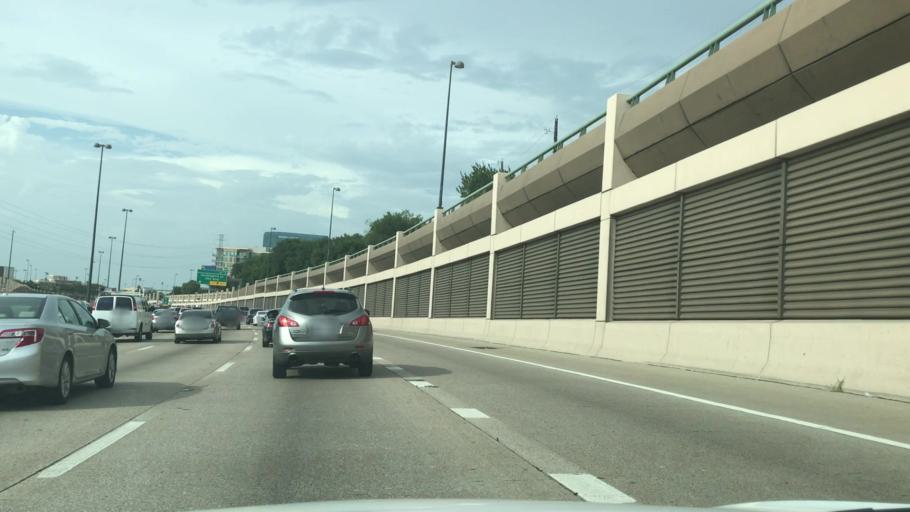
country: US
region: Texas
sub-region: Dallas County
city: Highland Park
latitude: 32.8303
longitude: -96.7807
